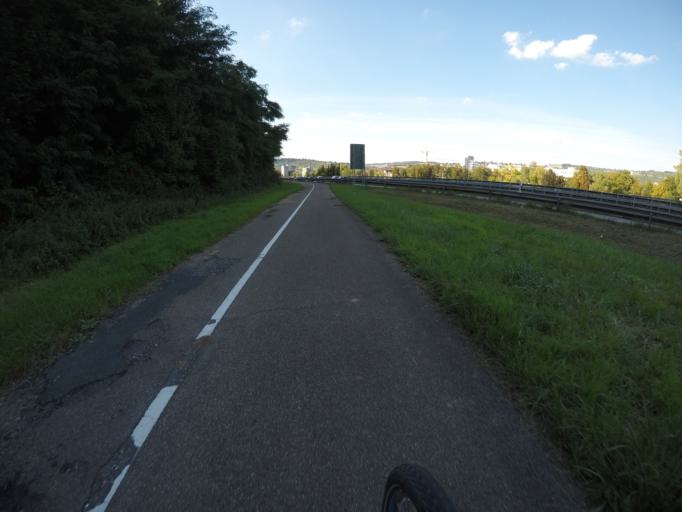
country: DE
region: Baden-Wuerttemberg
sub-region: Regierungsbezirk Stuttgart
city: Esslingen
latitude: 48.7278
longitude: 9.3178
